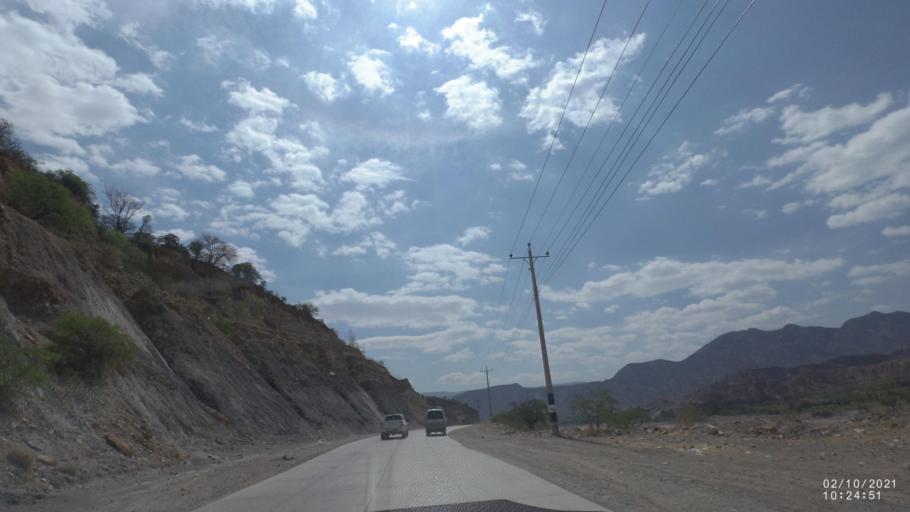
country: BO
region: Cochabamba
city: Irpa Irpa
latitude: -17.7252
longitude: -66.2719
